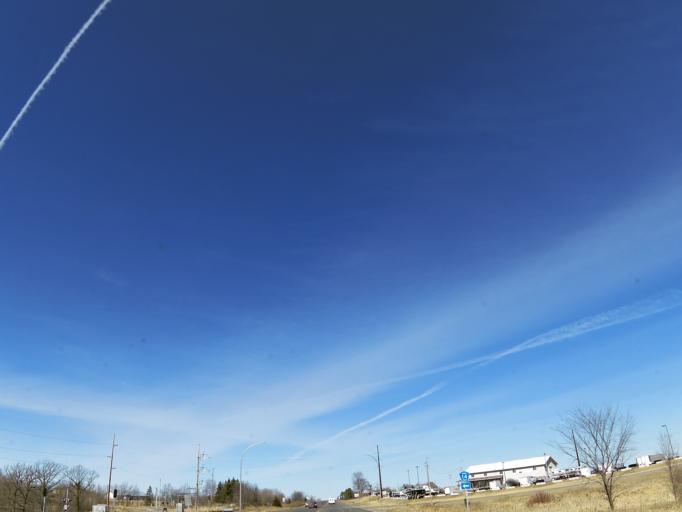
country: US
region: Minnesota
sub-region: Wright County
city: Buffalo
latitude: 45.1365
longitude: -93.8271
